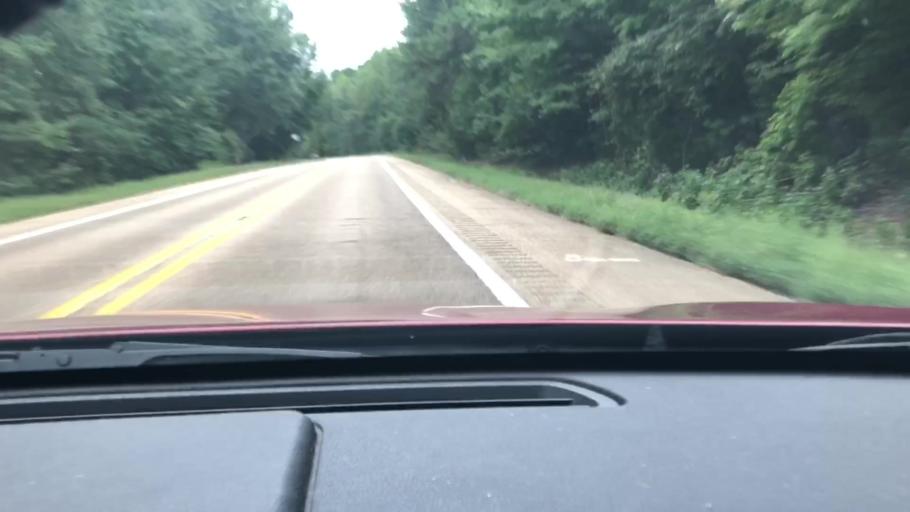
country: US
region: Arkansas
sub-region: Miller County
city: Texarkana
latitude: 33.4196
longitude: -93.8251
